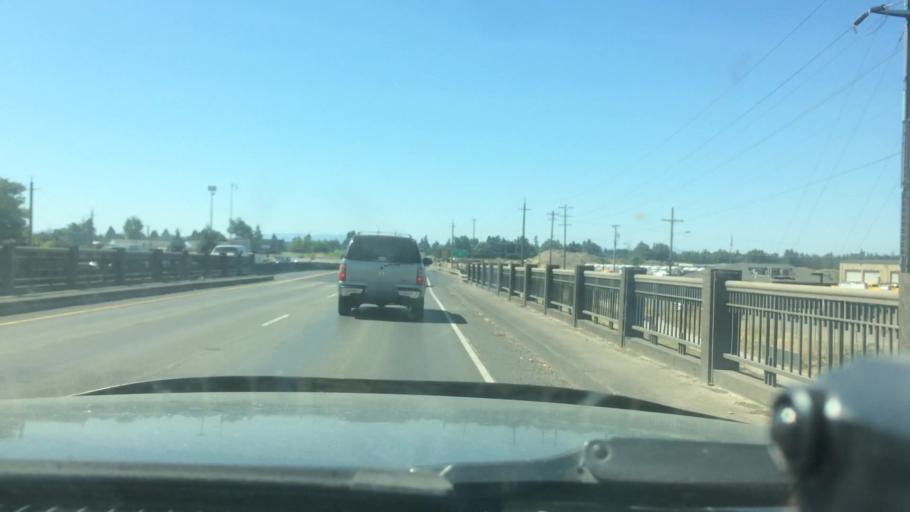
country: US
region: Oregon
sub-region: Lane County
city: Eugene
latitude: 44.0955
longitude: -123.1073
